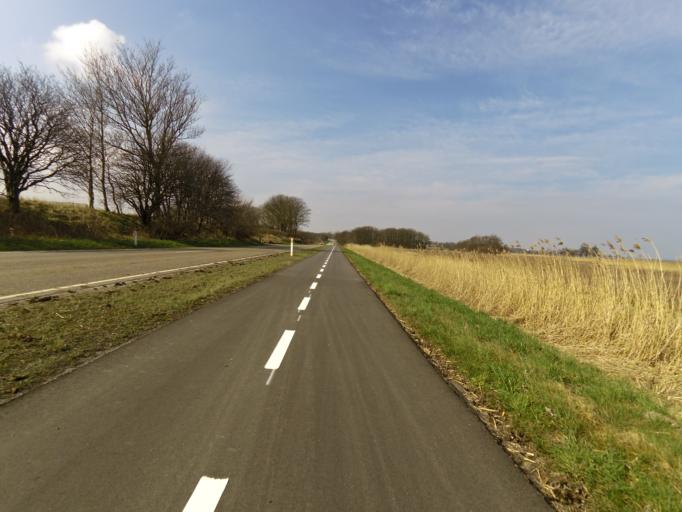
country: DK
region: Central Jutland
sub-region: Struer Kommune
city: Struer
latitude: 56.4734
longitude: 8.6218
